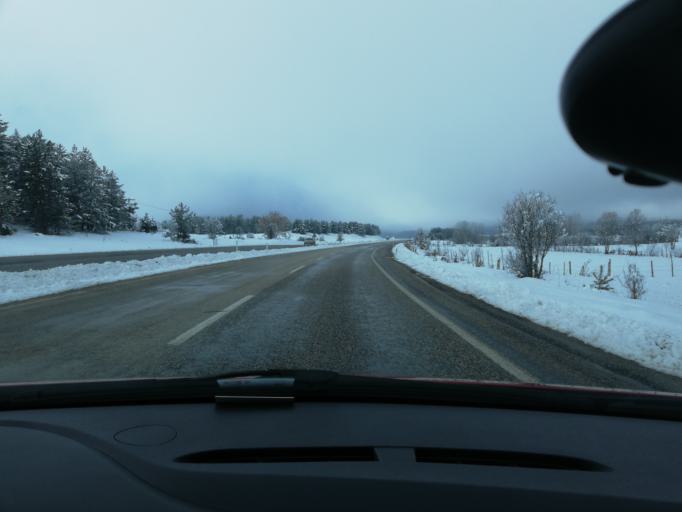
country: TR
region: Kastamonu
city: Ihsangazi
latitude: 41.3045
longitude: 33.5671
